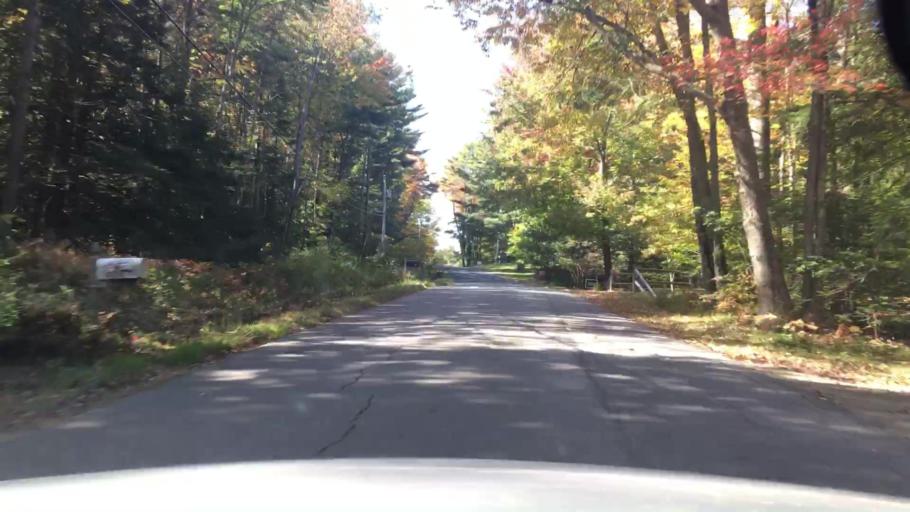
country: US
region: Maine
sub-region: Androscoggin County
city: Lisbon Falls
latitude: 44.0159
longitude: -69.9774
